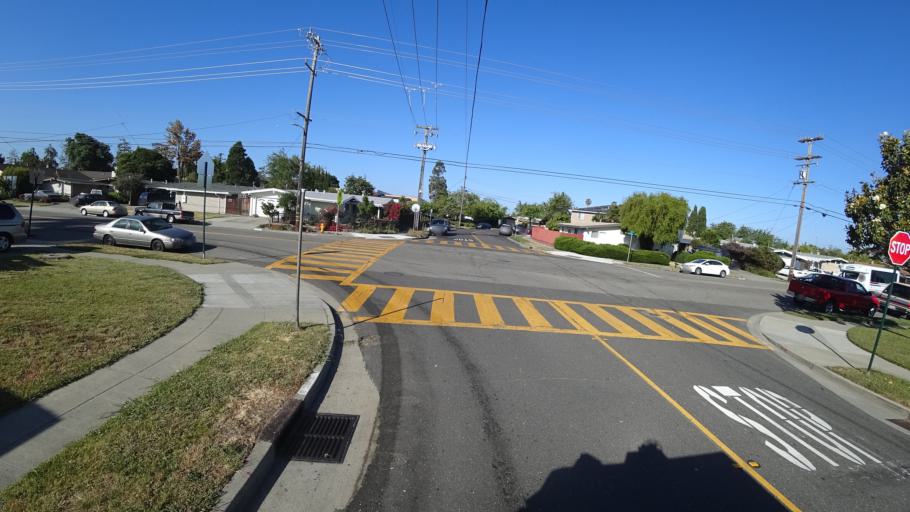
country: US
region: California
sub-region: Alameda County
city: Hayward
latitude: 37.6249
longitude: -122.1017
